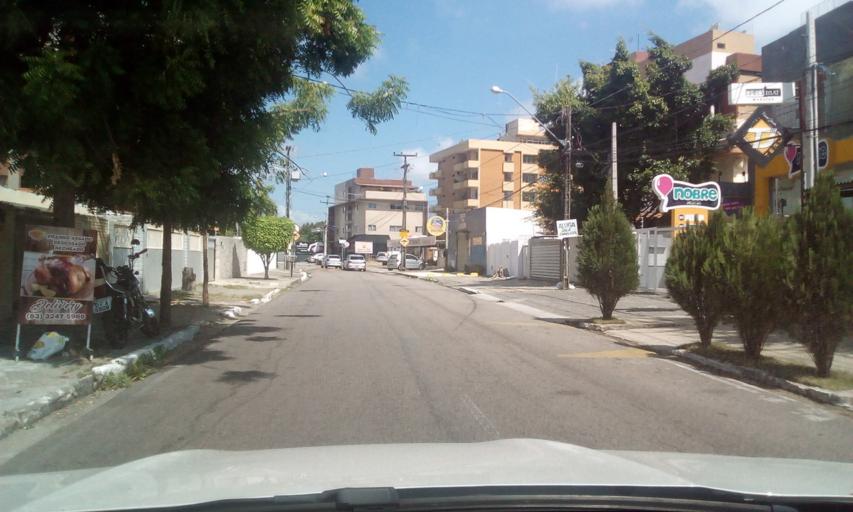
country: BR
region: Paraiba
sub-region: Joao Pessoa
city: Joao Pessoa
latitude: -7.1098
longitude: -34.8276
